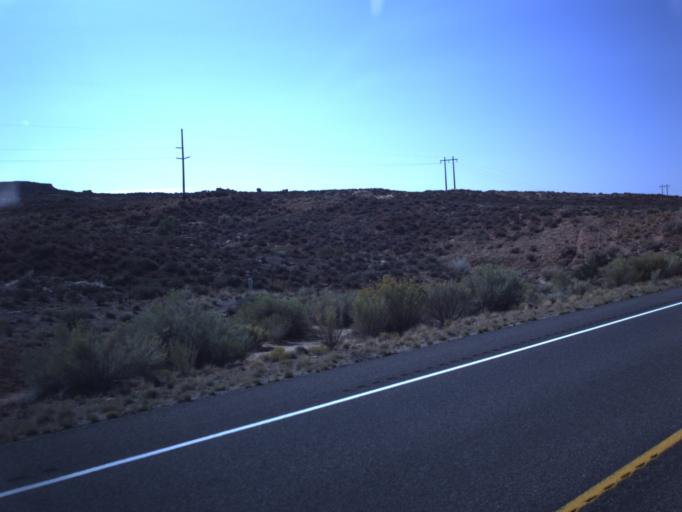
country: US
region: Utah
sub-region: San Juan County
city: Blanding
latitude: 37.3591
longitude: -109.5146
